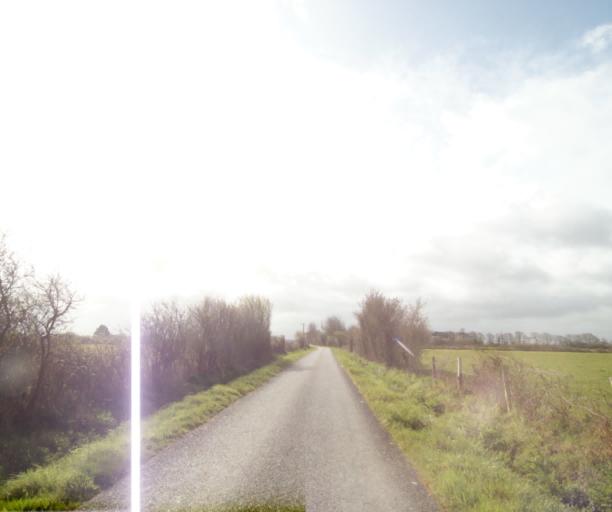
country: FR
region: Pays de la Loire
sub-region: Departement de la Loire-Atlantique
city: Bouvron
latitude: 47.4132
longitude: -1.8567
